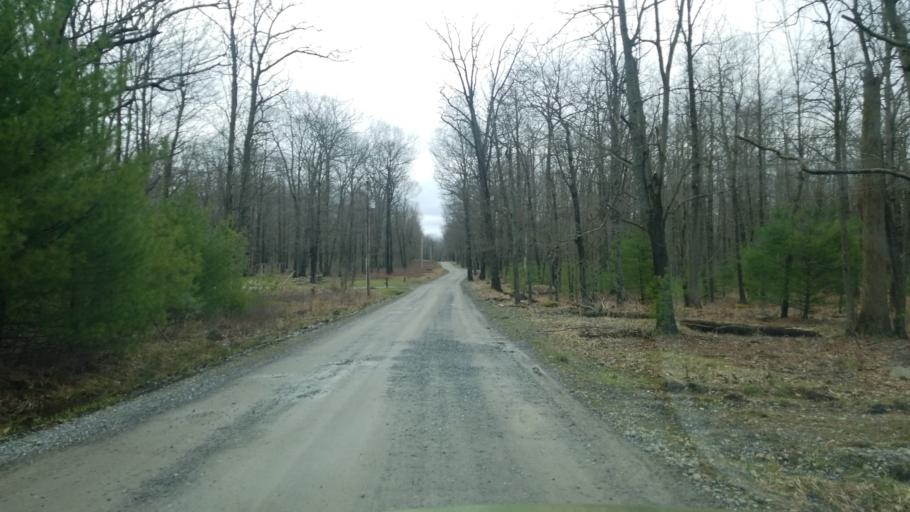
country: US
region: Pennsylvania
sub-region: Clearfield County
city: Shiloh
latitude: 41.1763
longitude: -78.3154
